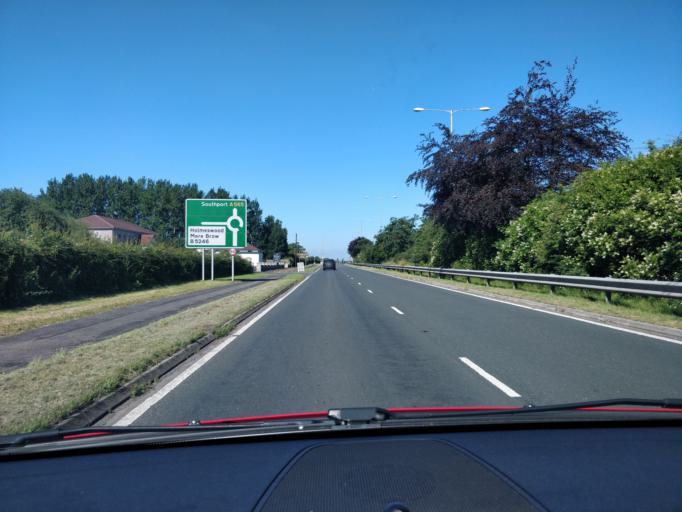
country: GB
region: England
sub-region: Lancashire
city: Banks
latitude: 53.6634
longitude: -2.8822
